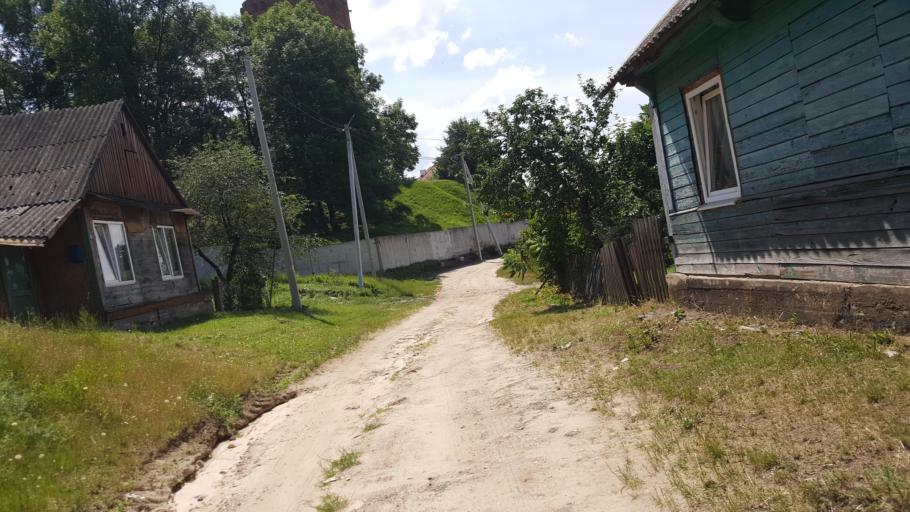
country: BY
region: Brest
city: Kamyanyets
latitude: 52.4053
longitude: 23.8203
